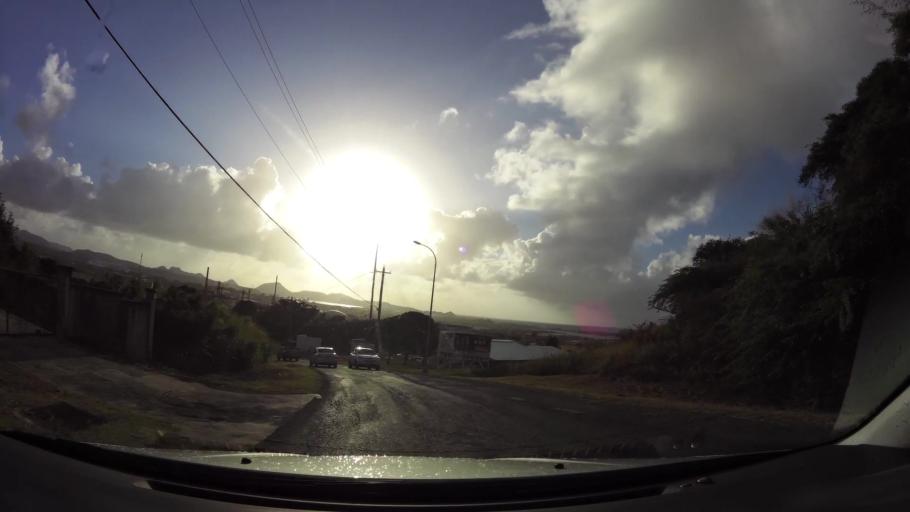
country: AG
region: Saint John
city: Saint John's
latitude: 17.1437
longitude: -61.8353
